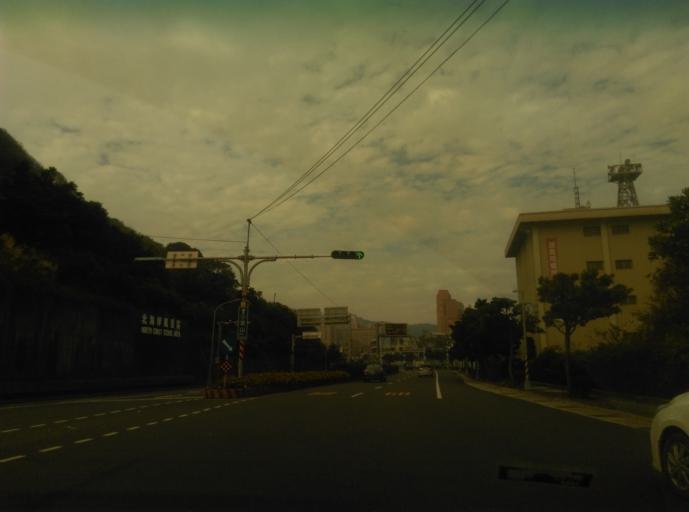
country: TW
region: Taiwan
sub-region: Keelung
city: Keelung
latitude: 25.1826
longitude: 121.6880
